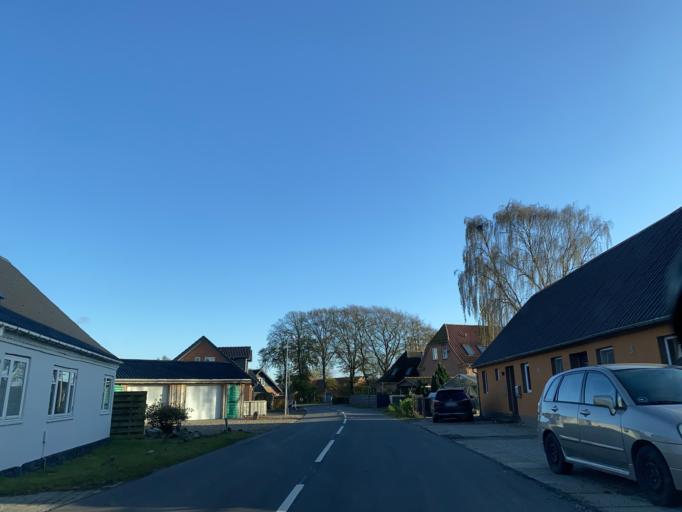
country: DK
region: Central Jutland
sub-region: Viborg Kommune
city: Bjerringbro
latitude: 56.3535
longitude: 9.6801
